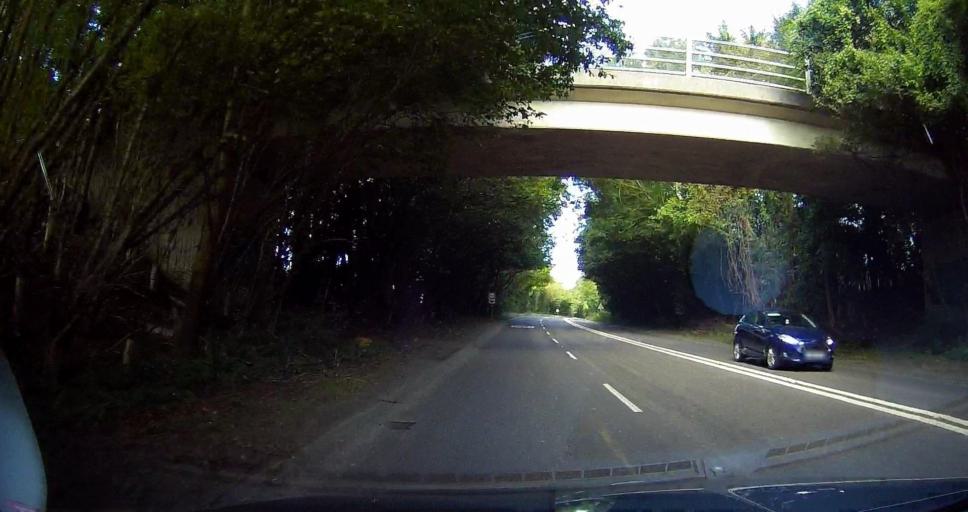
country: GB
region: England
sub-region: Kent
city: East Peckham
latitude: 51.2406
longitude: 0.3779
